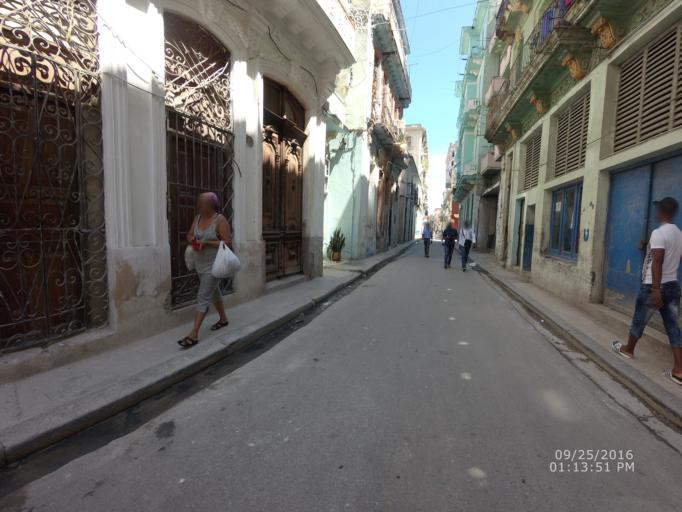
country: CU
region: La Habana
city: Centro Habana
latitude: 23.1388
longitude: -82.3566
